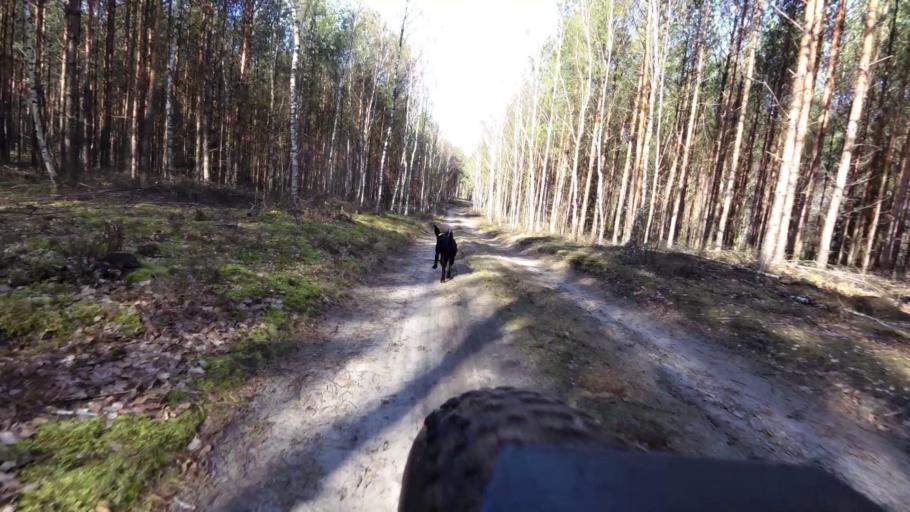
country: PL
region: Lubusz
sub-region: Powiat sulecinski
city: Torzym
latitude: 52.2190
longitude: 14.9926
